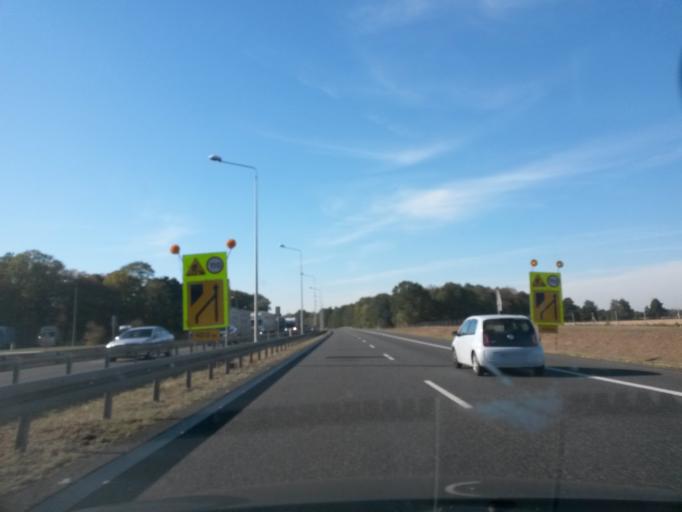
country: PL
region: Opole Voivodeship
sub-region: Powiat brzeski
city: Olszanka
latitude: 50.7651
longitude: 17.4132
